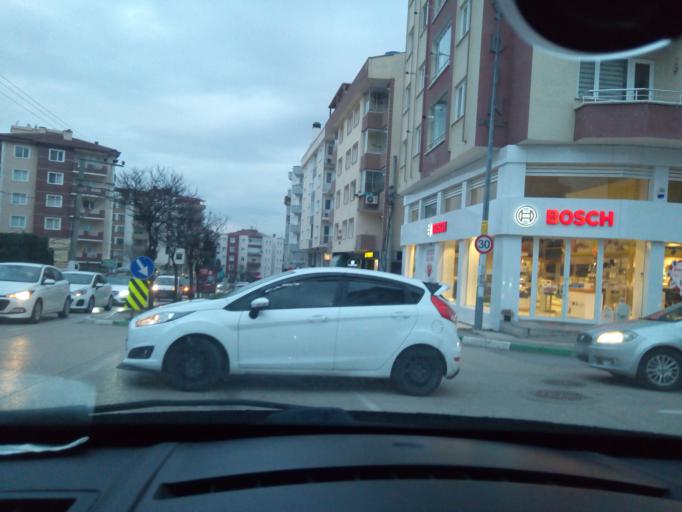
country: TR
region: Bursa
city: Yildirim
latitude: 40.2242
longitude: 28.9834
